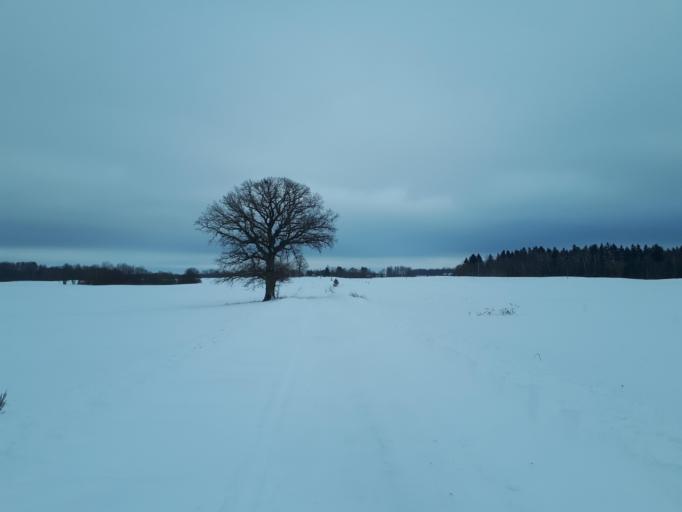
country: LT
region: Alytaus apskritis
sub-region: Alytaus rajonas
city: Daugai
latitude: 54.4536
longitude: 24.3492
